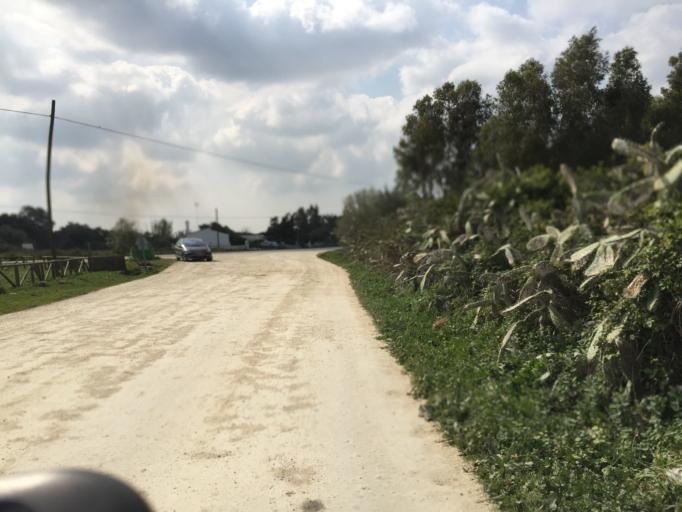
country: ES
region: Andalusia
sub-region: Provincia de Cadiz
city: Benalup-Casas Viejas
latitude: 36.3231
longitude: -5.8841
